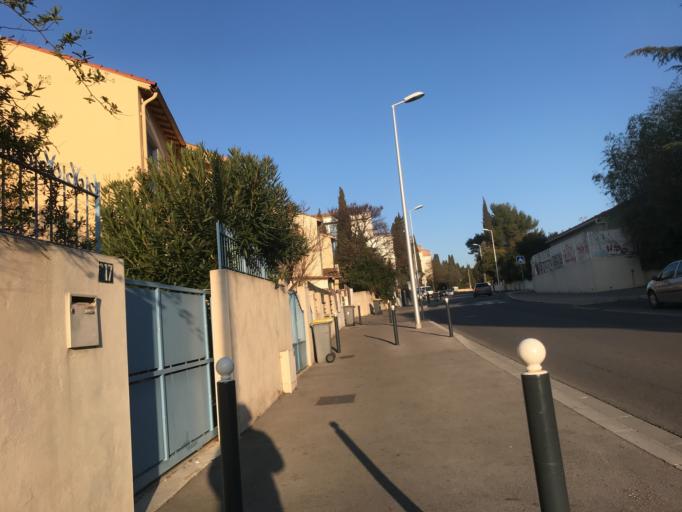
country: FR
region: Languedoc-Roussillon
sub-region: Departement de l'Herault
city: Montpellier
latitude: 43.6290
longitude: 3.8806
